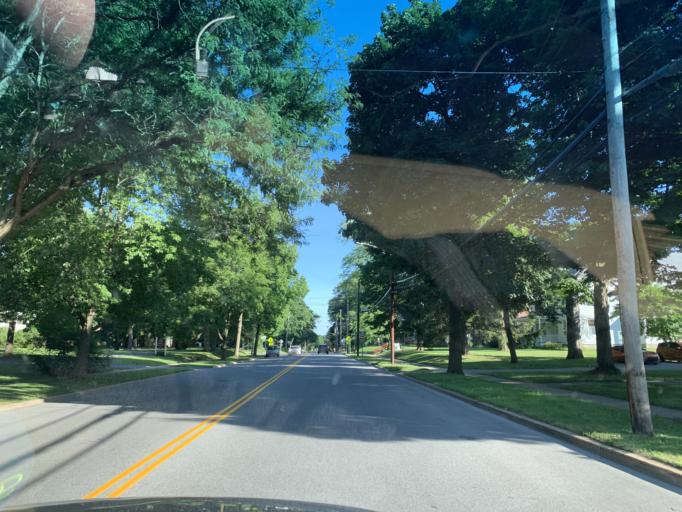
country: US
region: New York
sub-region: Madison County
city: Oneida
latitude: 43.0885
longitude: -75.6479
